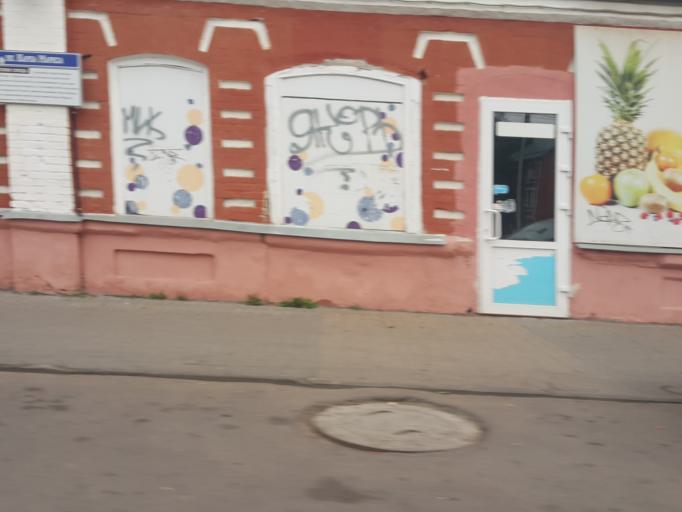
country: RU
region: Tambov
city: Tambov
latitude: 52.7121
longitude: 41.4573
